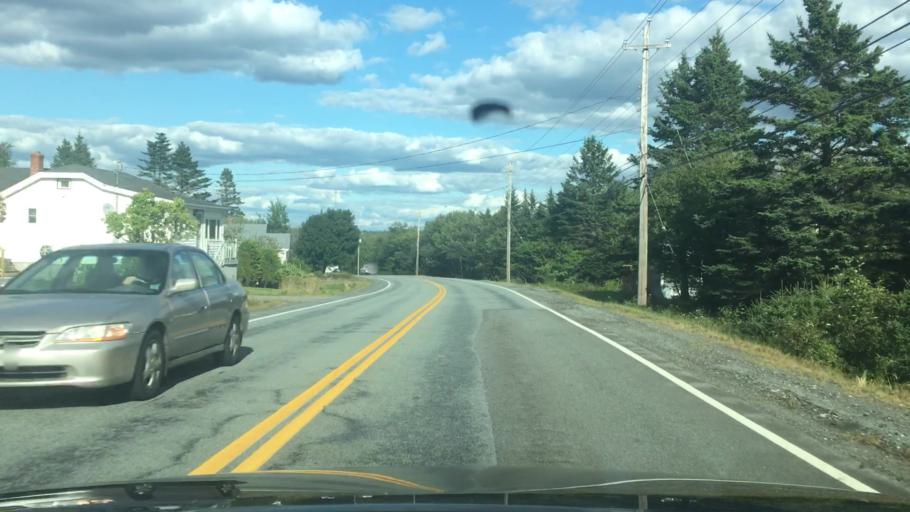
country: CA
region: Nova Scotia
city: Halifax
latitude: 44.5977
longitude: -63.6899
